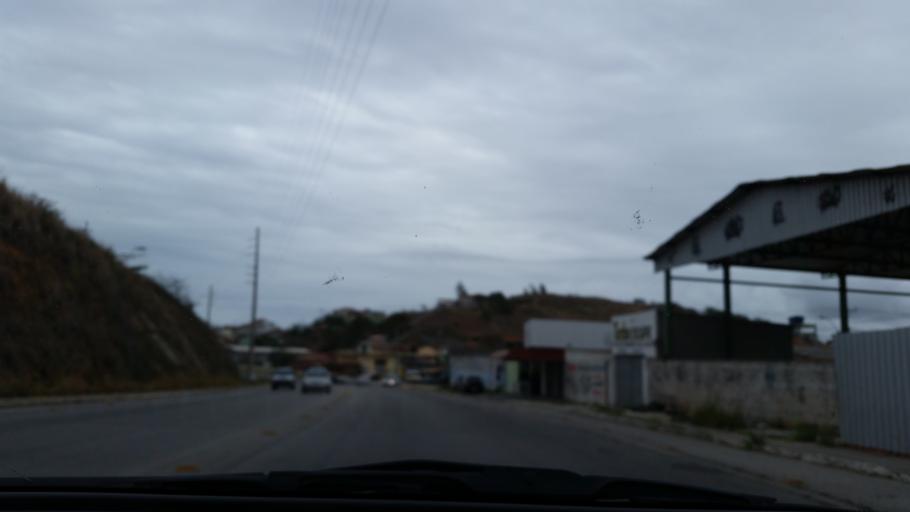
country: BR
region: Rio de Janeiro
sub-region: Cabo Frio
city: Cabo Frio
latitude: -22.8538
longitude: -42.0514
